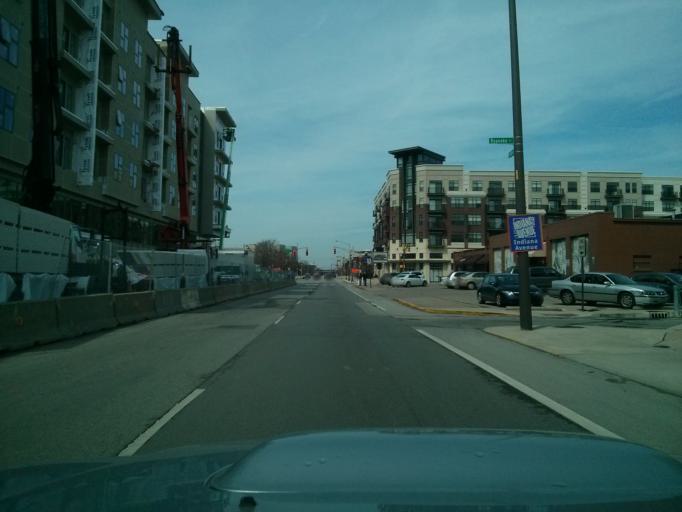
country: US
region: Indiana
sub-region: Marion County
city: Indianapolis
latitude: 39.7742
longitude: -86.1621
